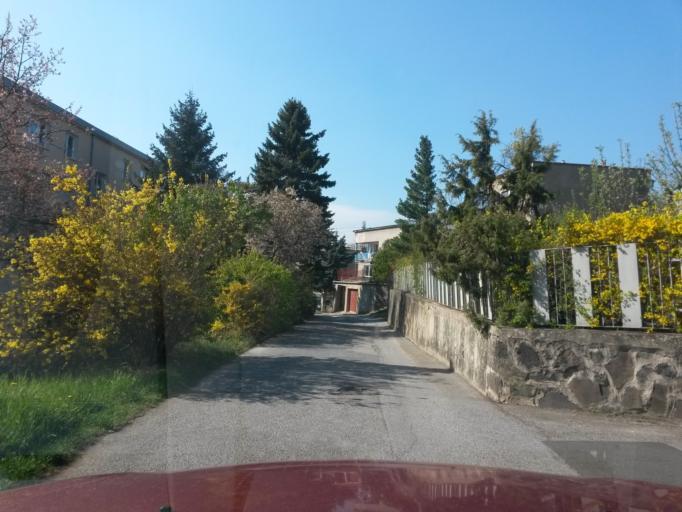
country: SK
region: Kosicky
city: Kosice
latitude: 48.7476
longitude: 21.2419
